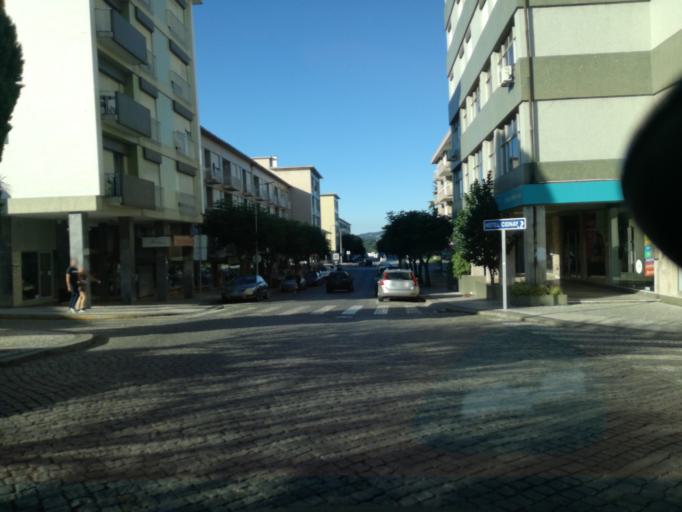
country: PT
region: Porto
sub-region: Santo Tirso
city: Santo Tirso
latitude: 41.3404
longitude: -8.4745
